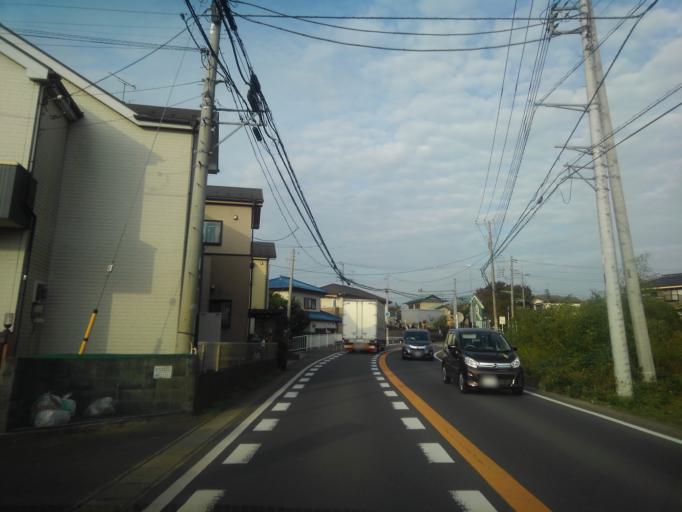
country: JP
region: Saitama
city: Sayama
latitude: 35.7895
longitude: 139.3938
